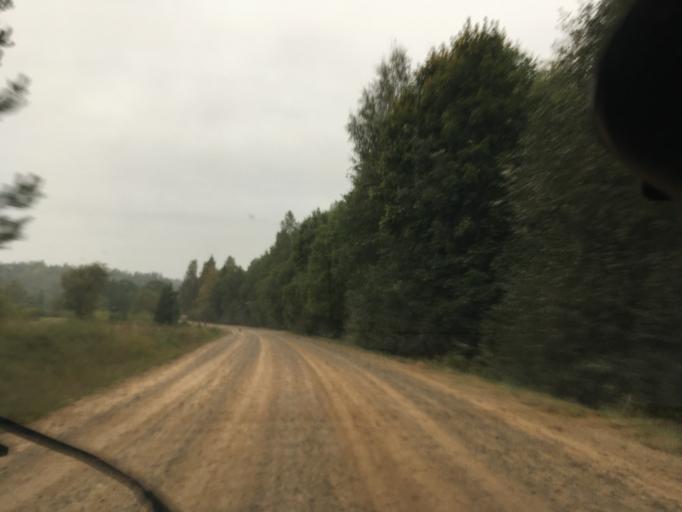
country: LV
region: Kuldigas Rajons
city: Kuldiga
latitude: 57.0039
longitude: 21.9797
